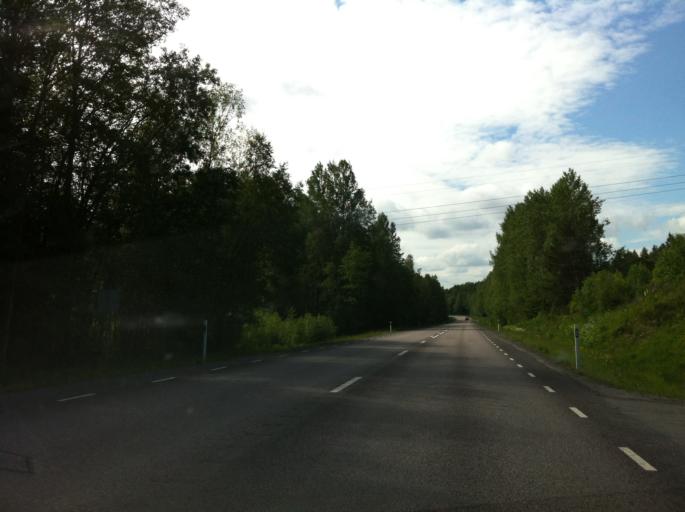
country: SE
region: Vaermland
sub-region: Karlstads Kommun
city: Valberg
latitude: 59.3918
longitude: 13.1779
